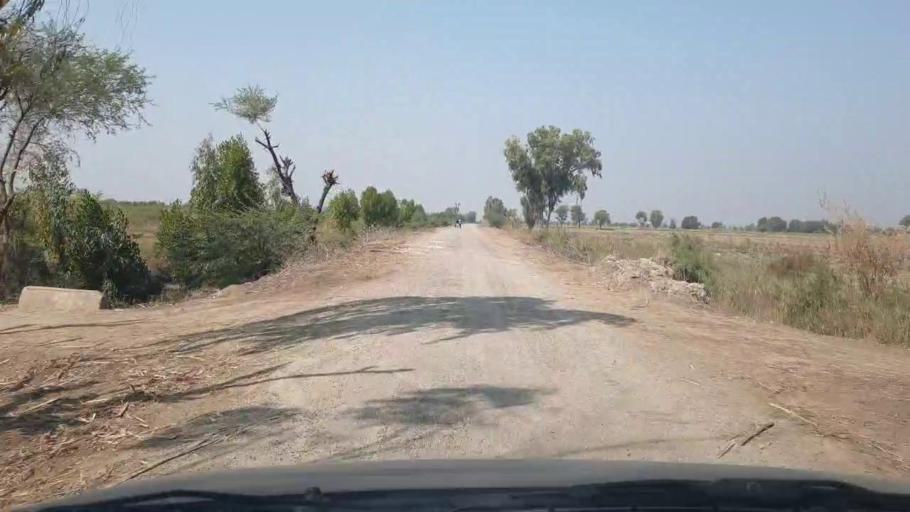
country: PK
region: Sindh
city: Mirwah Gorchani
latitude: 25.3425
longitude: 69.1444
